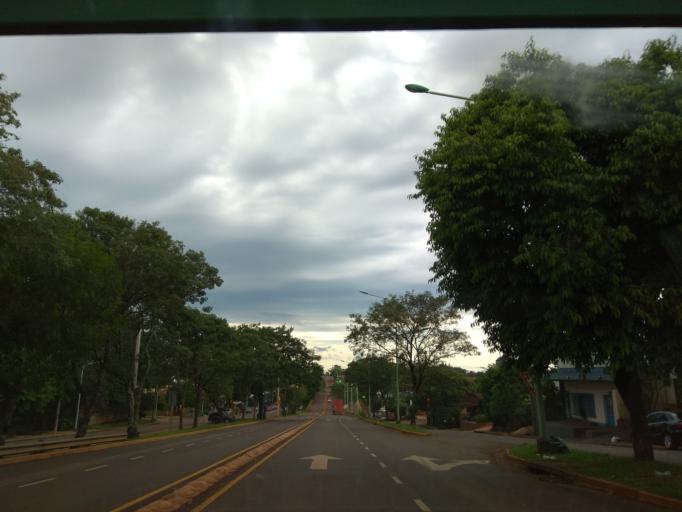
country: AR
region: Misiones
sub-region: Departamento de Leandro N. Alem
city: Leandro N. Alem
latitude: -27.6100
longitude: -55.3296
